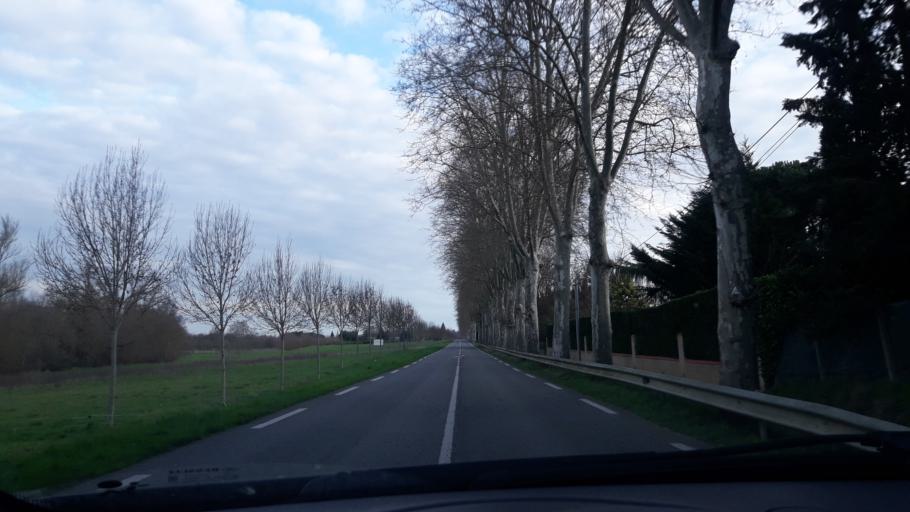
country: FR
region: Midi-Pyrenees
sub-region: Departement de la Haute-Garonne
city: Montaigut-sur-Save
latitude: 43.6954
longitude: 1.2355
